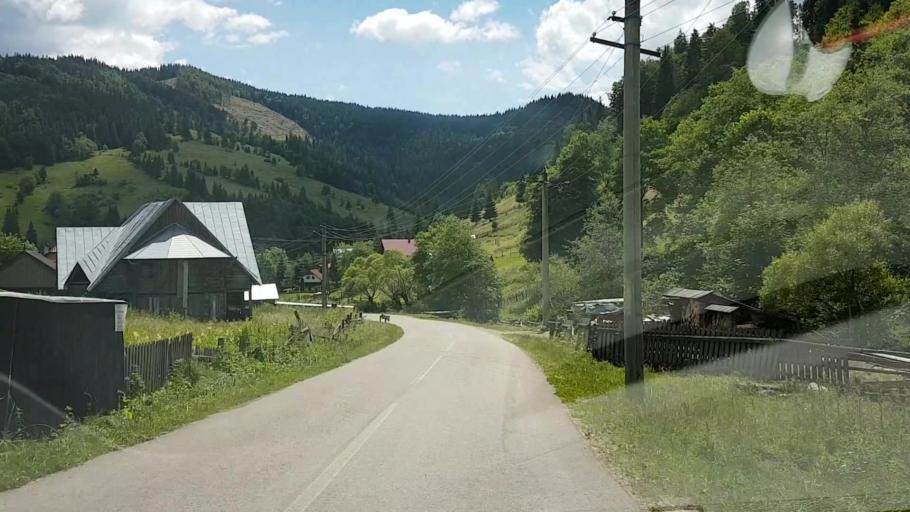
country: RO
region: Suceava
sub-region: Comuna Crucea
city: Crucea
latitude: 47.4197
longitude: 25.5807
